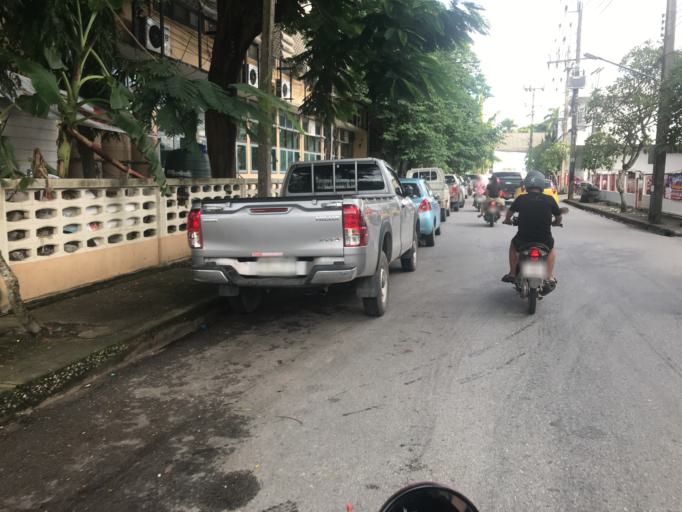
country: TH
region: Chiang Rai
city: Chiang Rai
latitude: 19.9115
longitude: 99.8311
